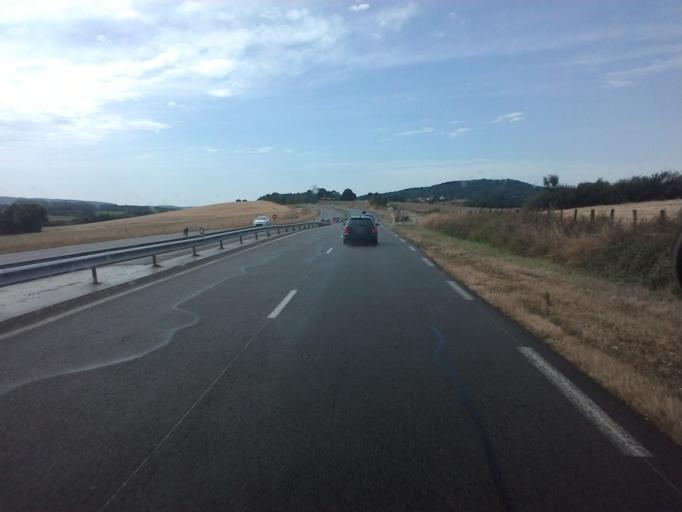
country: FR
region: Franche-Comte
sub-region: Departement du Jura
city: Montmorot
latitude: 46.7440
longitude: 5.5557
